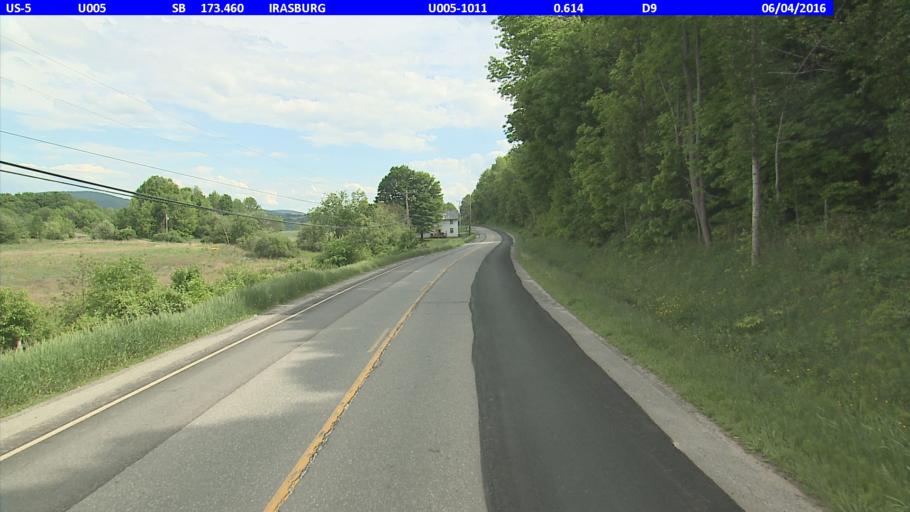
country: US
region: Vermont
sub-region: Orleans County
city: Newport
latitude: 44.8146
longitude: -72.2193
